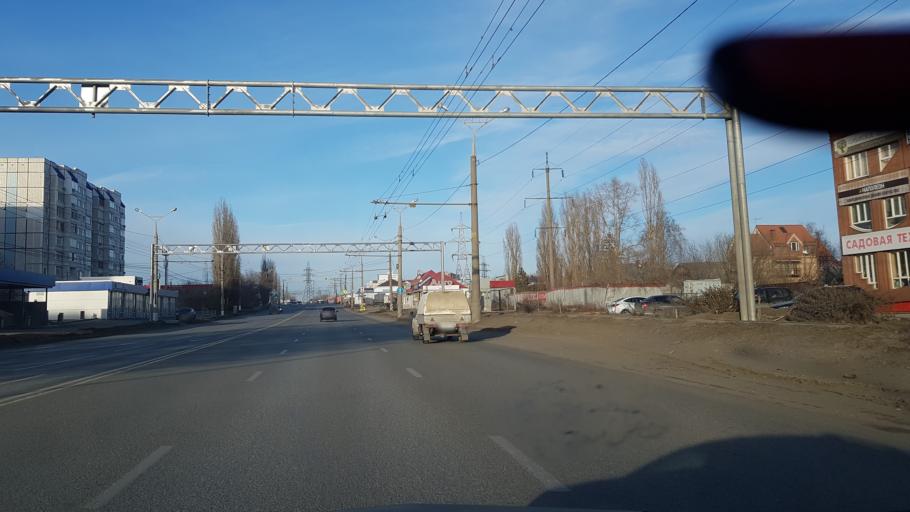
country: RU
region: Samara
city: Tol'yatti
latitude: 53.5316
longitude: 49.3965
